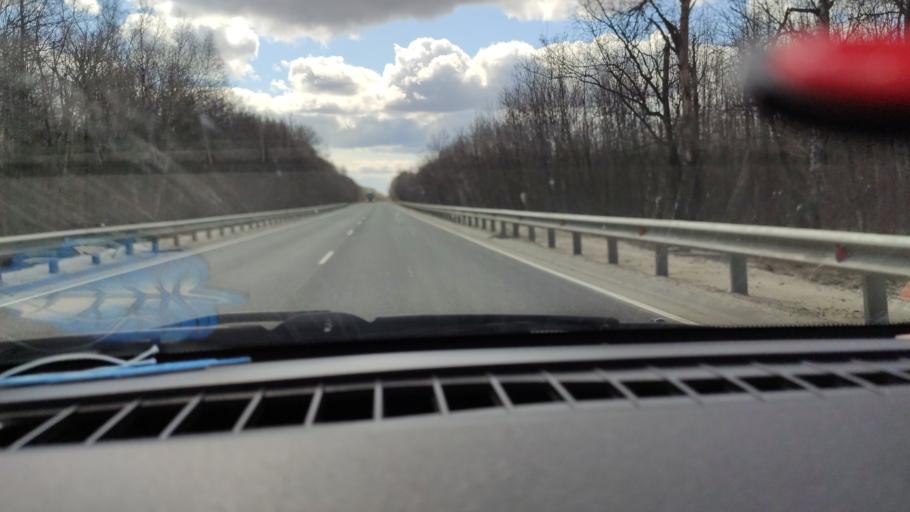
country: RU
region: Saratov
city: Khvalynsk
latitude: 52.4659
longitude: 48.0173
